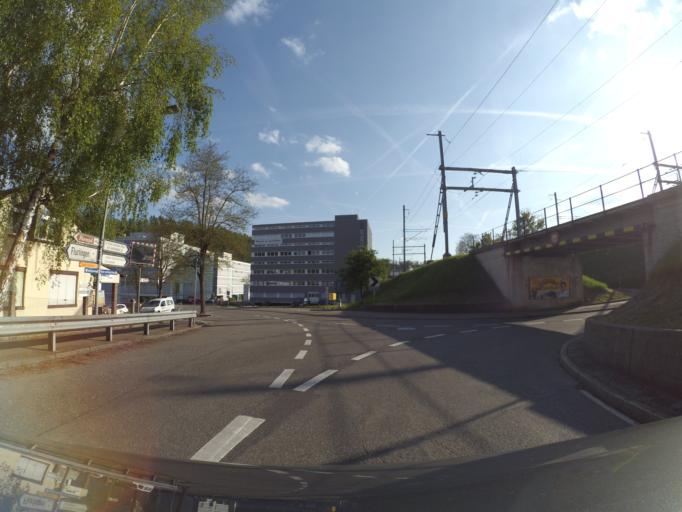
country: CH
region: Zurich
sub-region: Bezirk Andelfingen
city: Flurlingen
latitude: 47.6798
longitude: 8.6253
